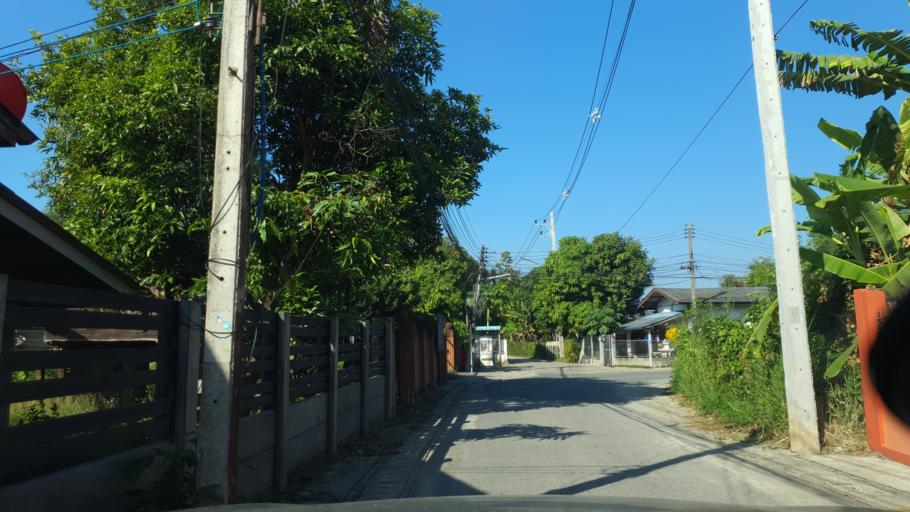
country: TH
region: Chiang Mai
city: San Kamphaeng
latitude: 18.7341
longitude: 99.1378
